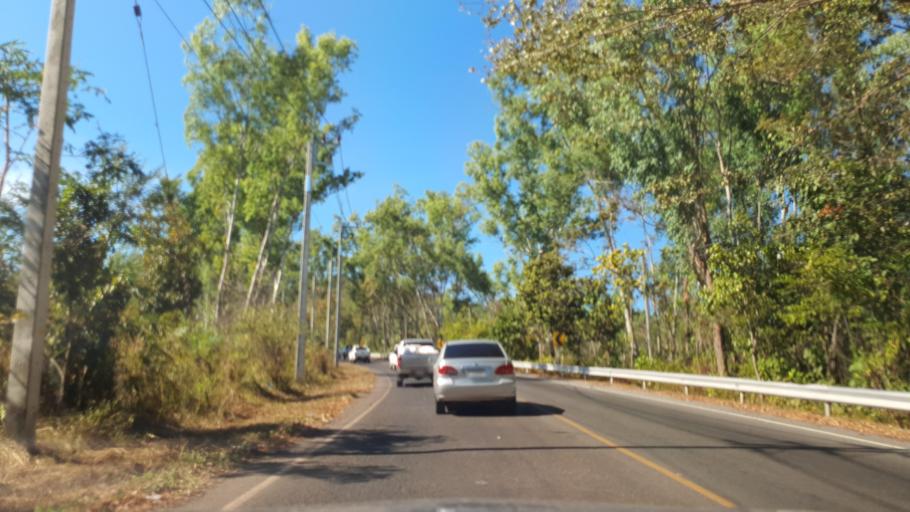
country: TH
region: Kalasin
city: Khao Wong
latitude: 16.7650
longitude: 104.1398
